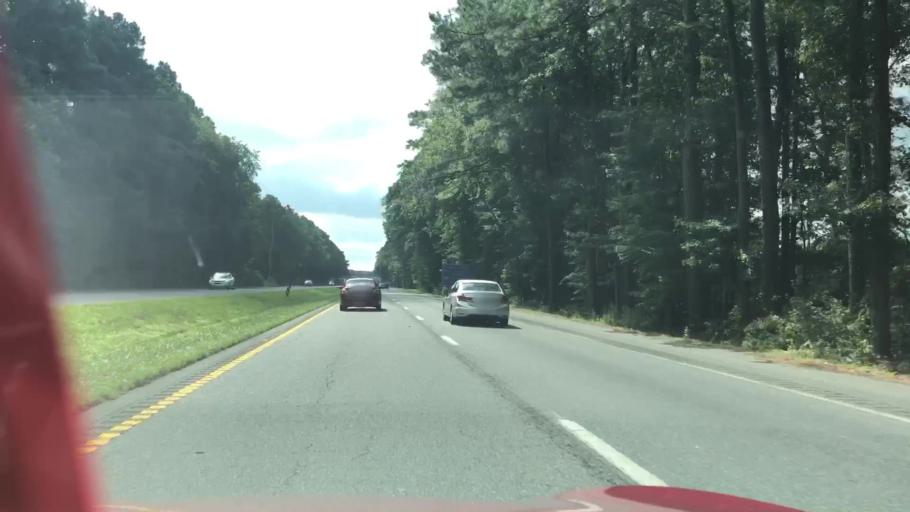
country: US
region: Virginia
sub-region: Accomack County
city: Wattsville
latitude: 37.9946
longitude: -75.5371
